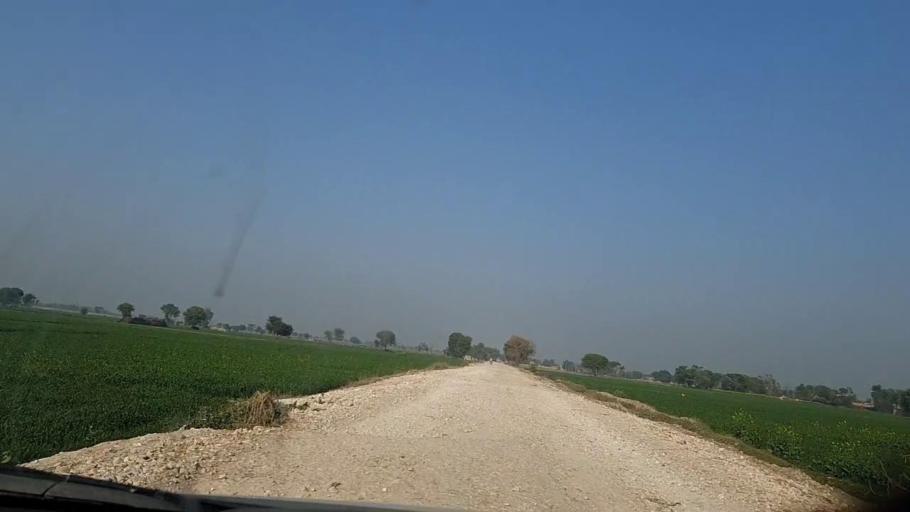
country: PK
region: Sindh
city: Moro
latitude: 26.7718
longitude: 67.9321
